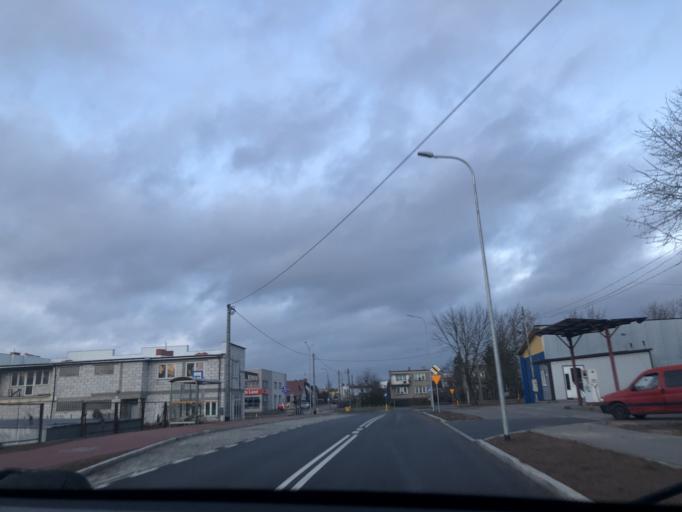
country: PL
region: Podlasie
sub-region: Lomza
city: Lomza
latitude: 53.1739
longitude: 22.0639
